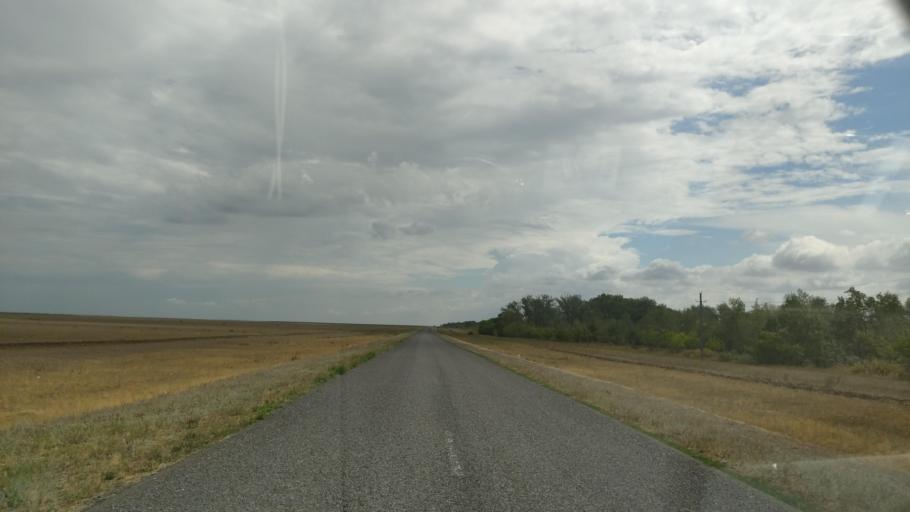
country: KZ
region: Pavlodar
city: Pavlodar
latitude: 52.6439
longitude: 77.0494
